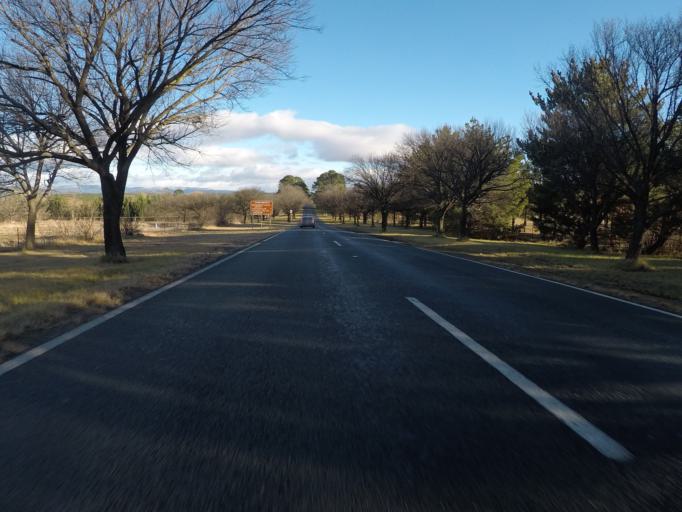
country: AU
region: Australian Capital Territory
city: Forrest
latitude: -35.3119
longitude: 149.0814
